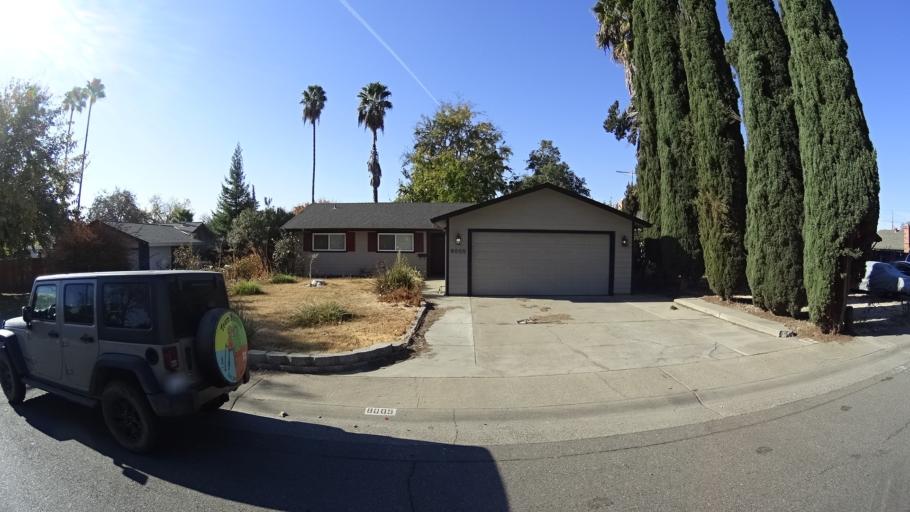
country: US
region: California
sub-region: Sacramento County
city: Antelope
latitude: 38.7107
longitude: -121.3074
